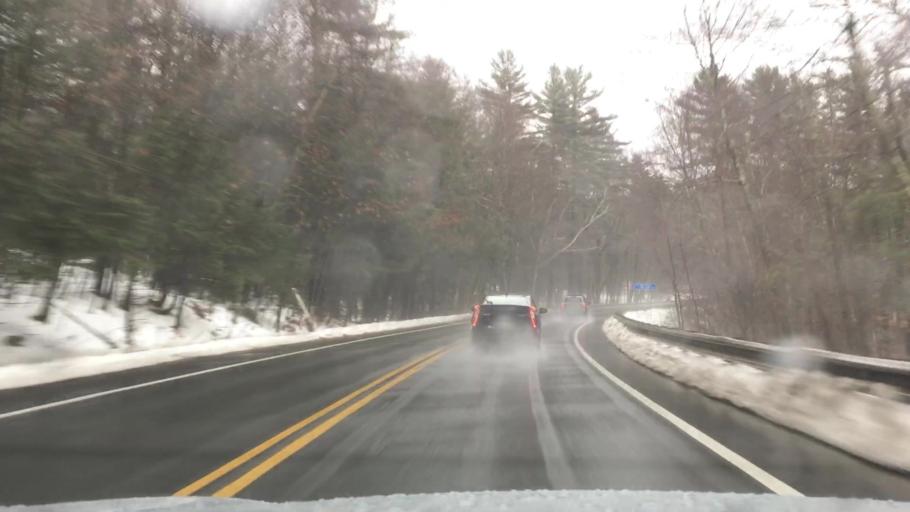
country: US
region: Massachusetts
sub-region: Franklin County
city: Shutesbury
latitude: 42.4475
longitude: -72.3883
